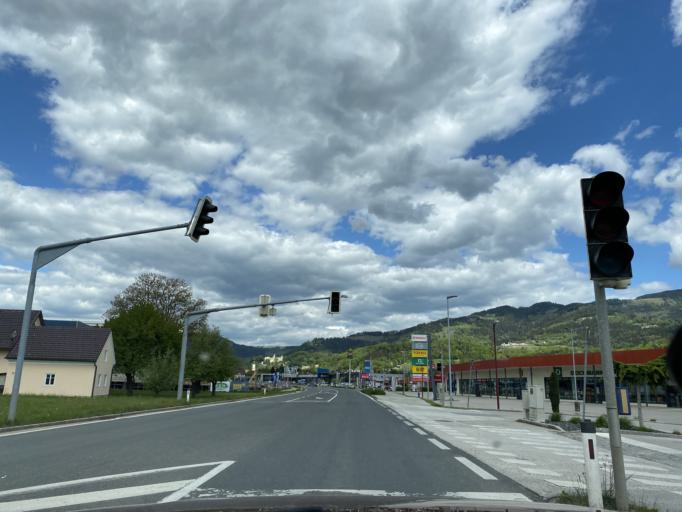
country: AT
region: Carinthia
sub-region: Politischer Bezirk Wolfsberg
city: Wolfsberg
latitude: 46.8219
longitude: 14.8379
